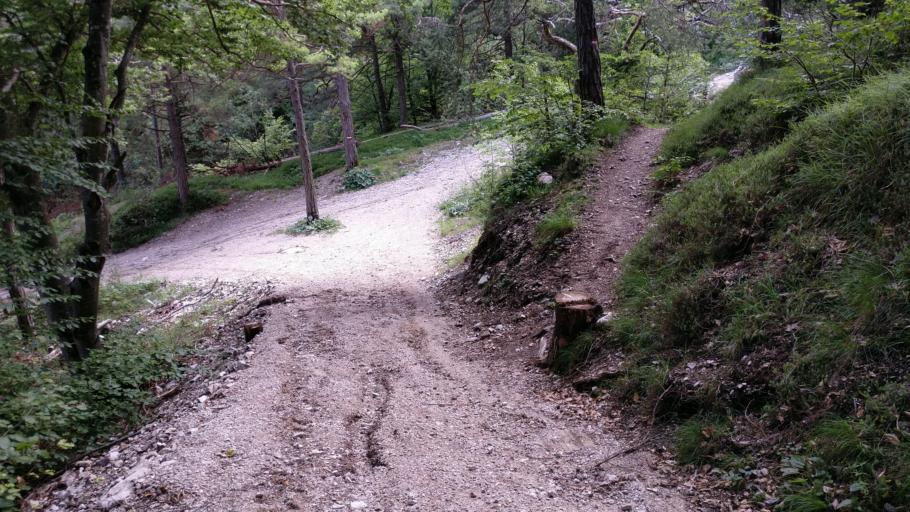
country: IT
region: Trentino-Alto Adige
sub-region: Bolzano
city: San Michele
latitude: 46.4531
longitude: 11.2261
